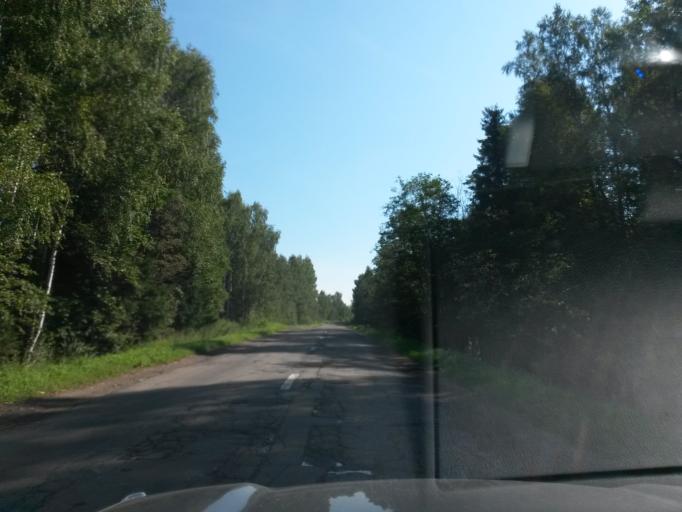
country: RU
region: Jaroslavl
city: Gavrilov-Yam
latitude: 57.3021
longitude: 40.0113
